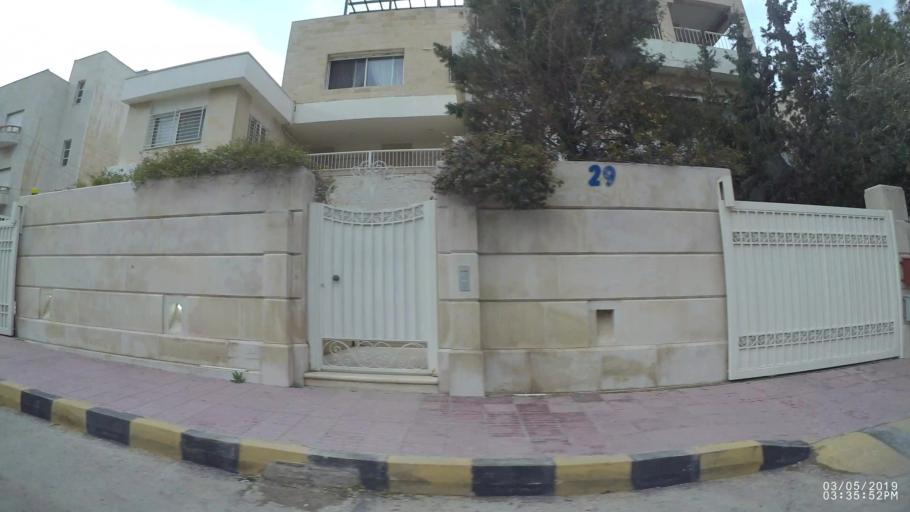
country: JO
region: Amman
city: Amman
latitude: 32.0049
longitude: 35.9439
